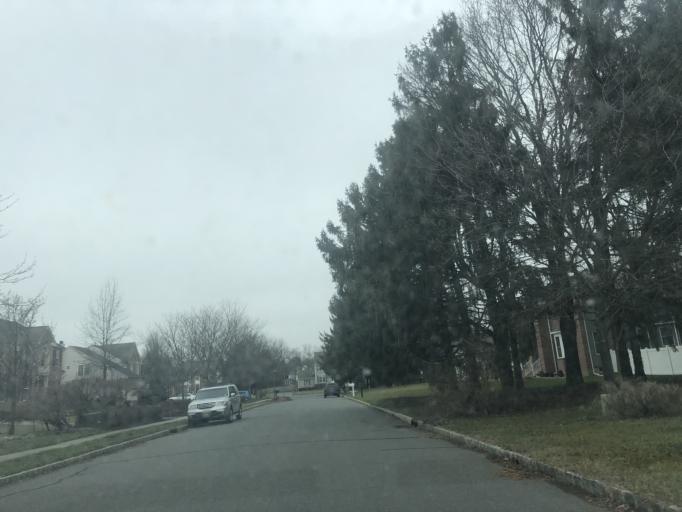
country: US
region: New Jersey
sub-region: Monmouth County
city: Allentown
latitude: 40.1972
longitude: -74.5999
